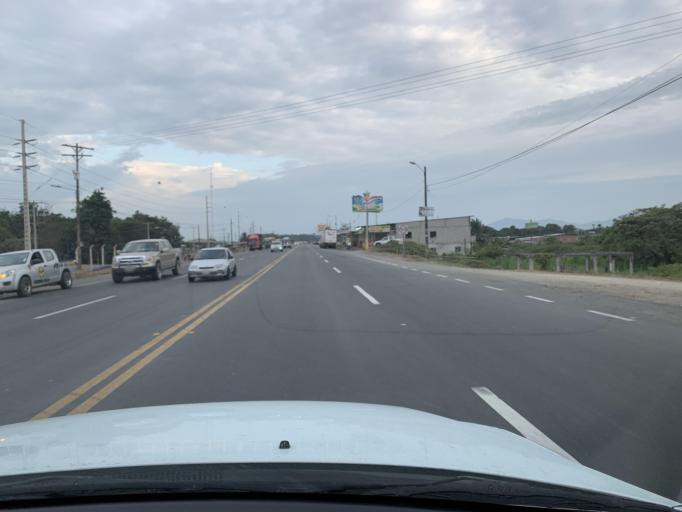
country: EC
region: Guayas
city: Yaguachi Nuevo
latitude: -2.2405
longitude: -79.6381
